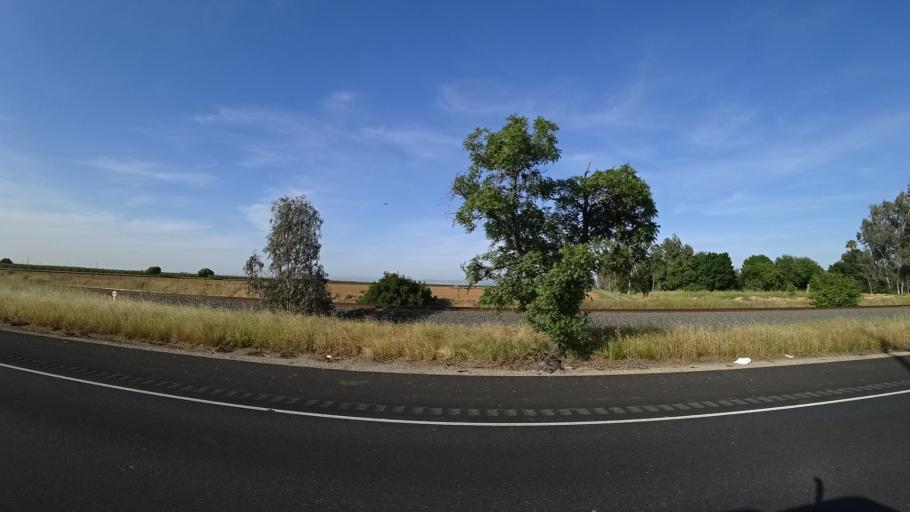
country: US
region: California
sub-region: Yuba County
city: Wheatland
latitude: 39.0247
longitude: -121.4486
